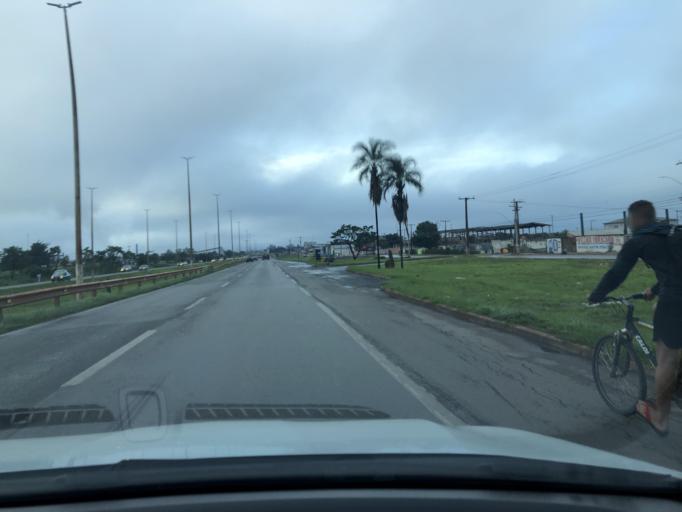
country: BR
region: Goias
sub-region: Luziania
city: Luziania
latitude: -16.1161
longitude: -47.9676
